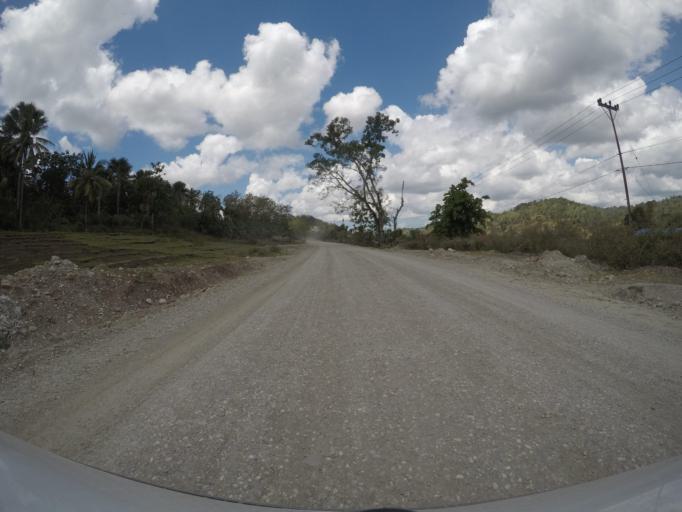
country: TL
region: Viqueque
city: Viqueque
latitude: -8.8221
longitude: 126.3783
